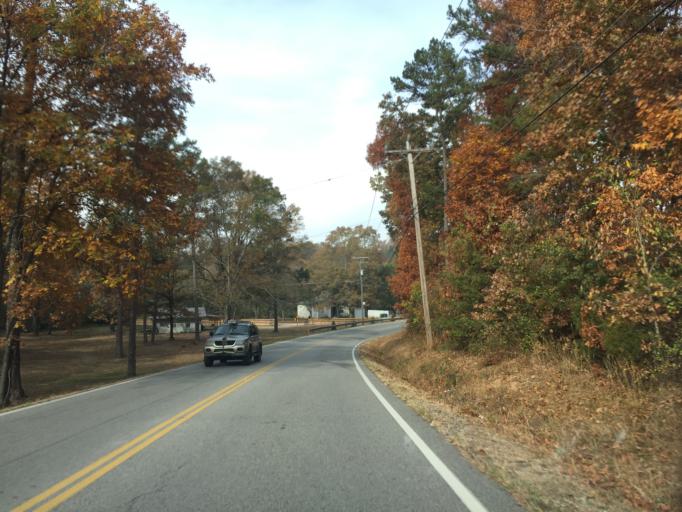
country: US
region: Tennessee
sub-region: Hamilton County
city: Harrison
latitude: 35.1078
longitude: -85.0827
